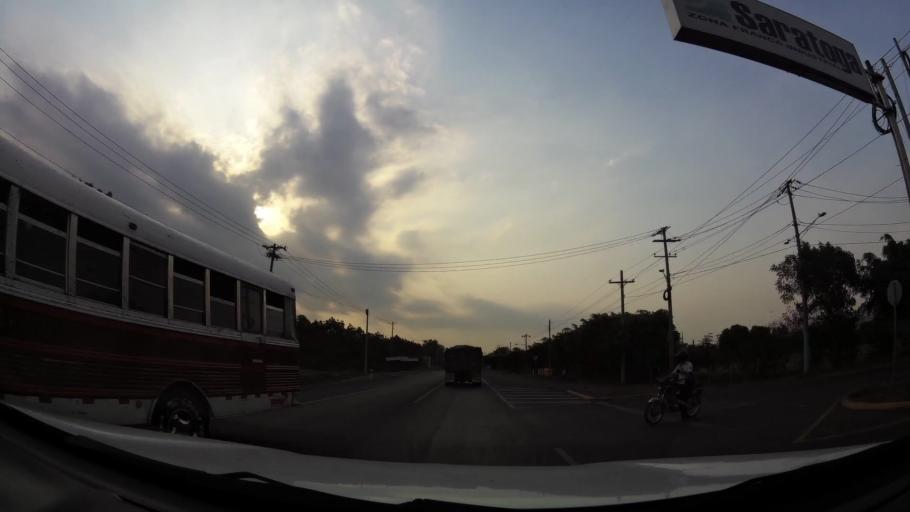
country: NI
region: Managua
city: Ciudad Sandino
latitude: 12.1811
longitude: -86.3563
